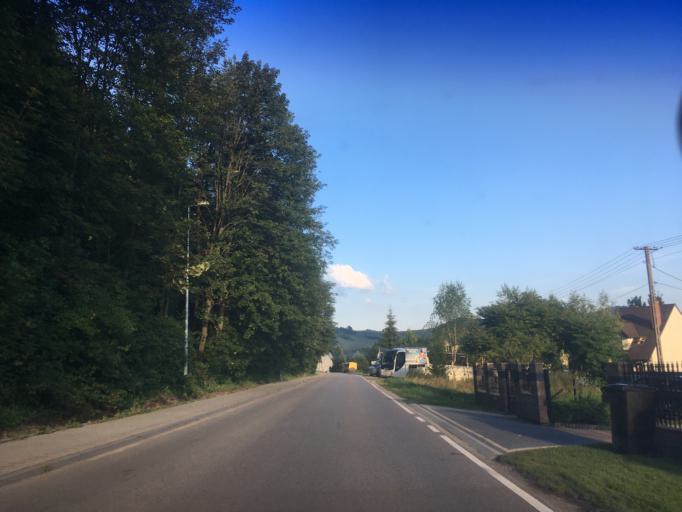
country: PL
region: Lesser Poland Voivodeship
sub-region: Powiat nowotarski
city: Kroscienko nad Dunajcem
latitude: 49.3939
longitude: 20.3906
